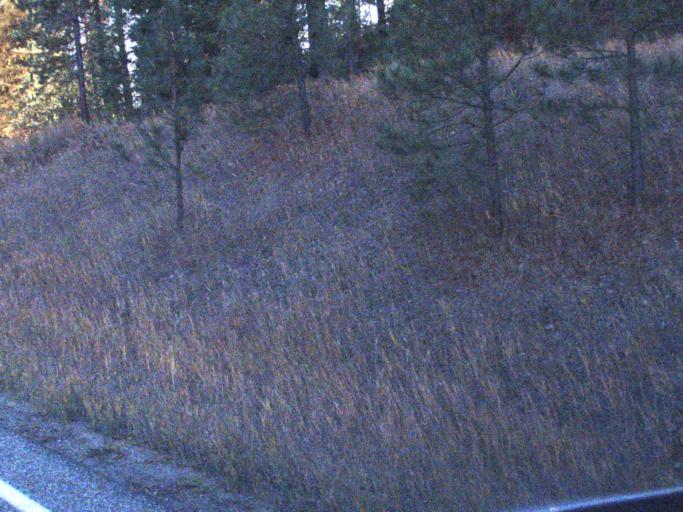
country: CA
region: British Columbia
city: Rossland
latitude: 48.9319
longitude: -117.7729
